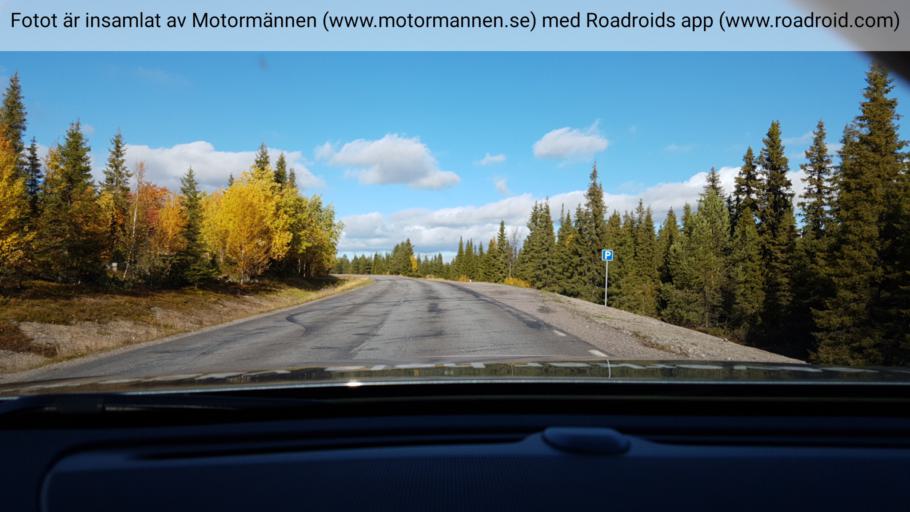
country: SE
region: Norrbotten
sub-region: Arjeplogs Kommun
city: Arjeplog
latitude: 65.9023
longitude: 18.3610
